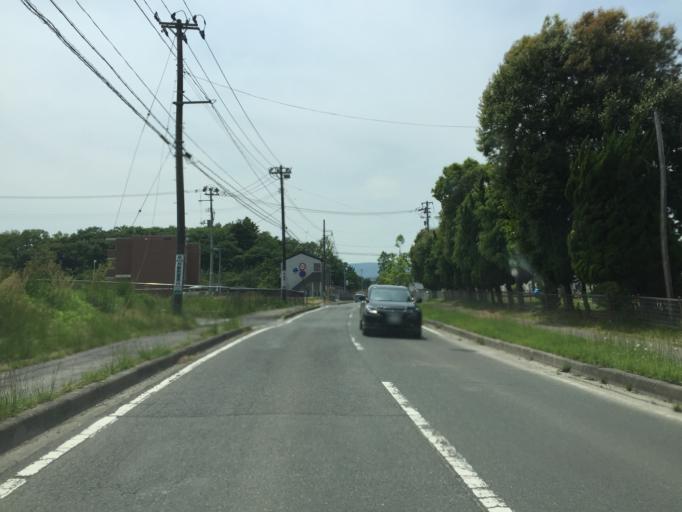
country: JP
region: Miyagi
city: Marumori
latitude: 37.8132
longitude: 140.9276
